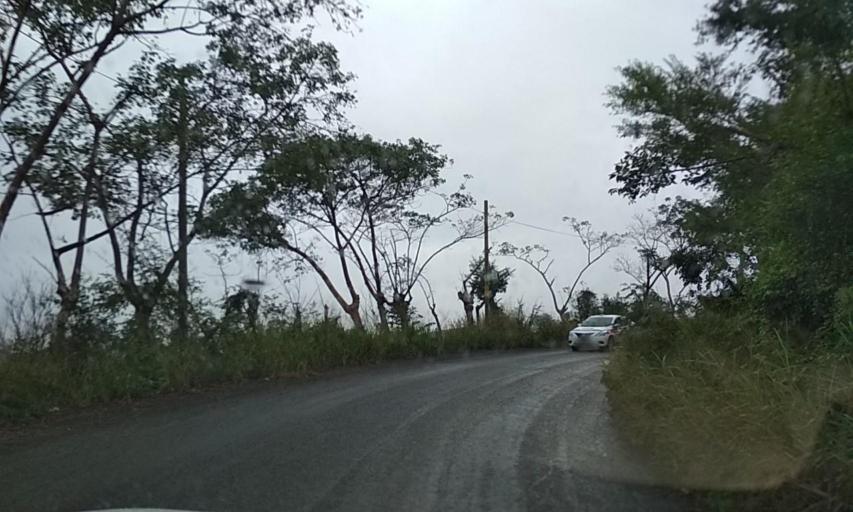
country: MX
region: Veracruz
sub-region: Coatzintla
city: Manuel Maria Contreras
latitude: 20.4586
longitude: -97.4727
